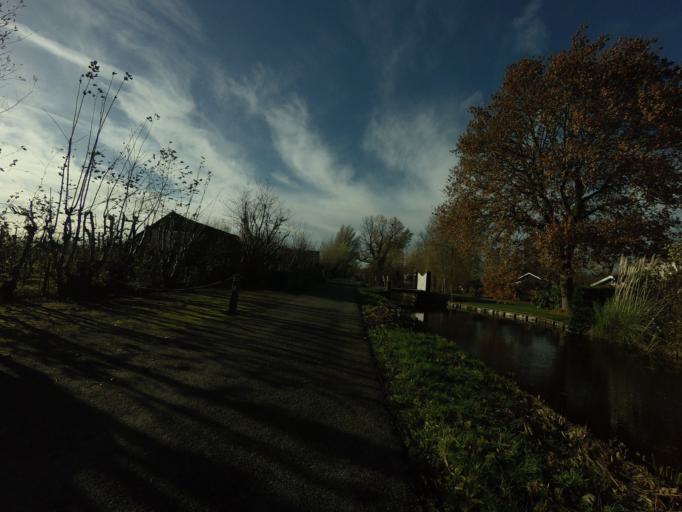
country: NL
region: South Holland
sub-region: Gemeente Vlist
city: Haastrecht
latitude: 52.0202
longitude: 4.7665
